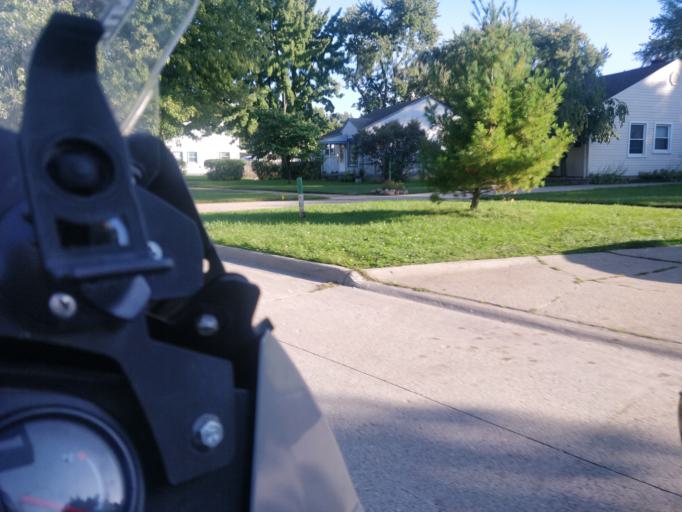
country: US
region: Michigan
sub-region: Wayne County
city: Melvindale
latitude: 42.2936
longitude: -83.1838
